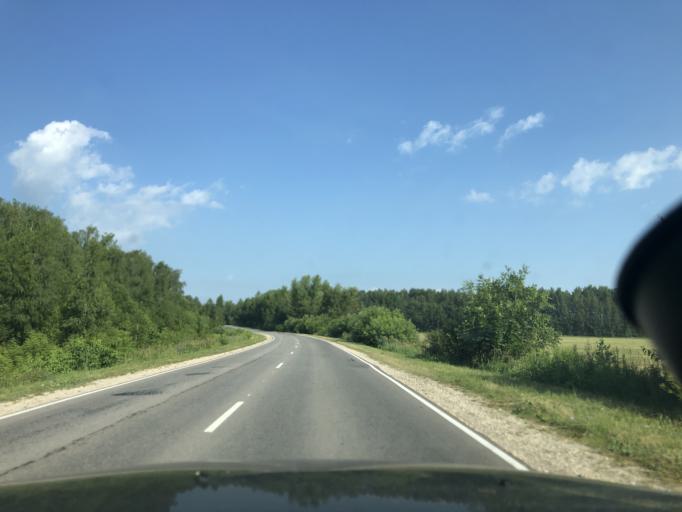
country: RU
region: Tula
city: Dubna
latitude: 54.1212
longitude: 37.0756
